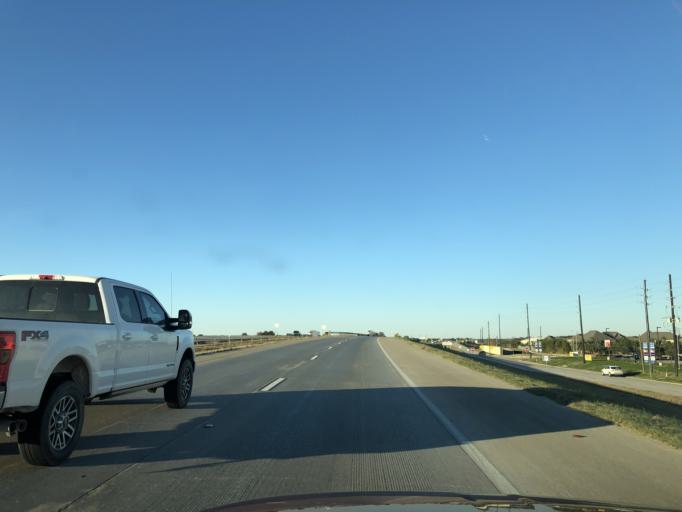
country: US
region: Texas
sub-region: Harris County
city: Cypress
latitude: 30.0131
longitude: -95.7690
